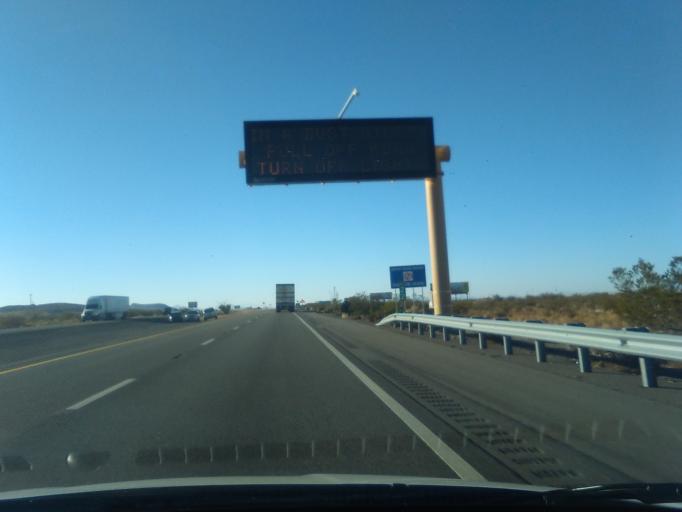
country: US
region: New Mexico
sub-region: Hidalgo County
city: Lordsburg
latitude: 32.3460
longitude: -108.7220
